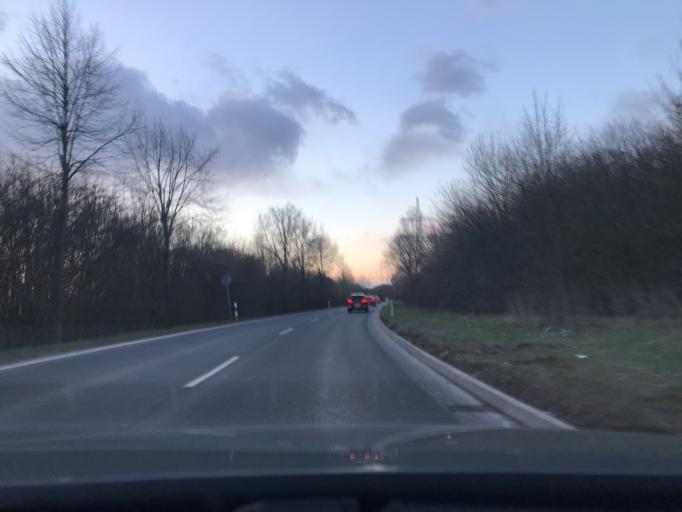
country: DE
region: North Rhine-Westphalia
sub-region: Regierungsbezirk Dusseldorf
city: Kaarst
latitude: 51.2599
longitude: 6.6130
